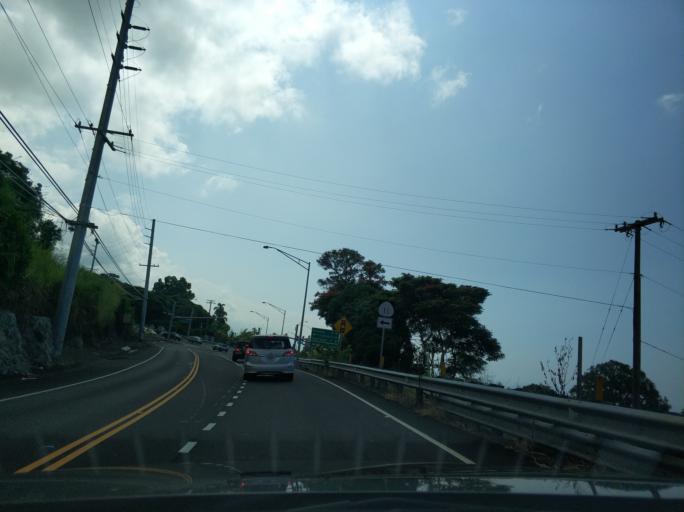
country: US
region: Hawaii
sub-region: Hawaii County
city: Captain Cook
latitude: 19.4947
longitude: -155.9187
